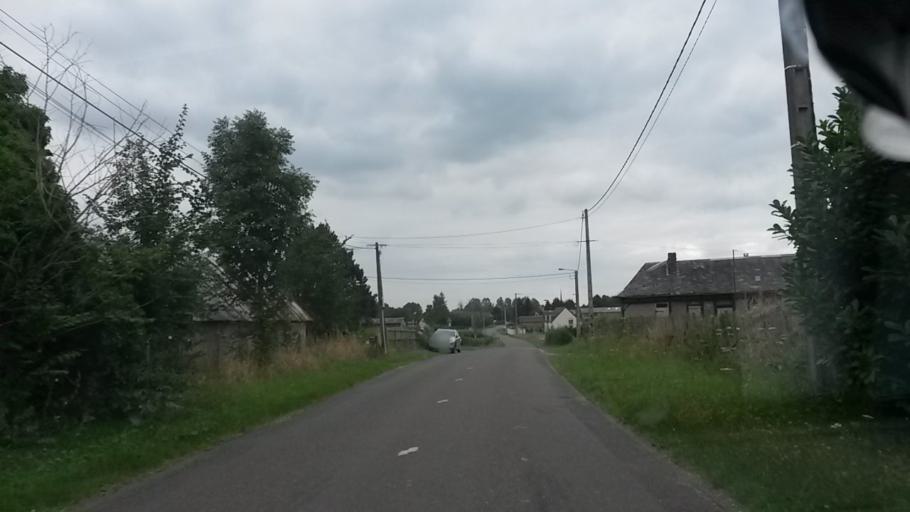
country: FR
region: Haute-Normandie
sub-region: Departement de la Seine-Maritime
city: La Feuillie
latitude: 49.4720
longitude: 1.5285
